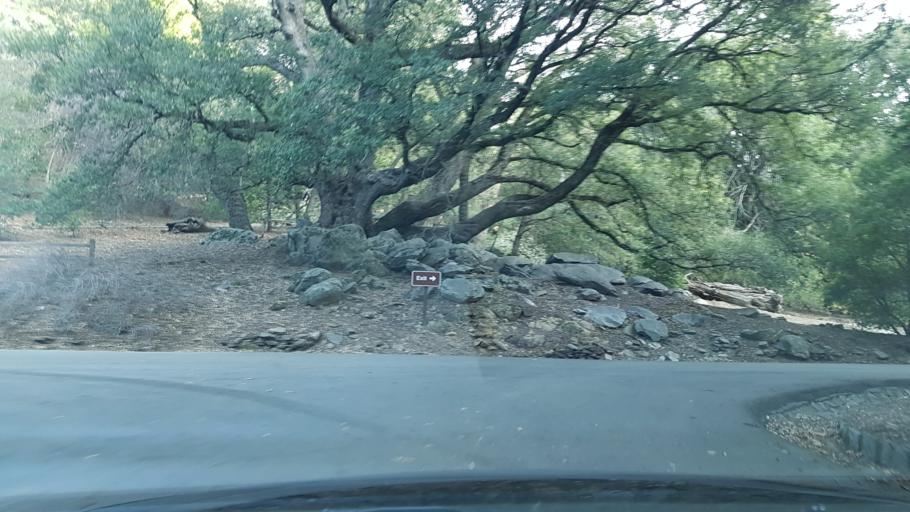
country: US
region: California
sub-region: Riverside County
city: Aguanga
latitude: 33.3431
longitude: -116.9016
